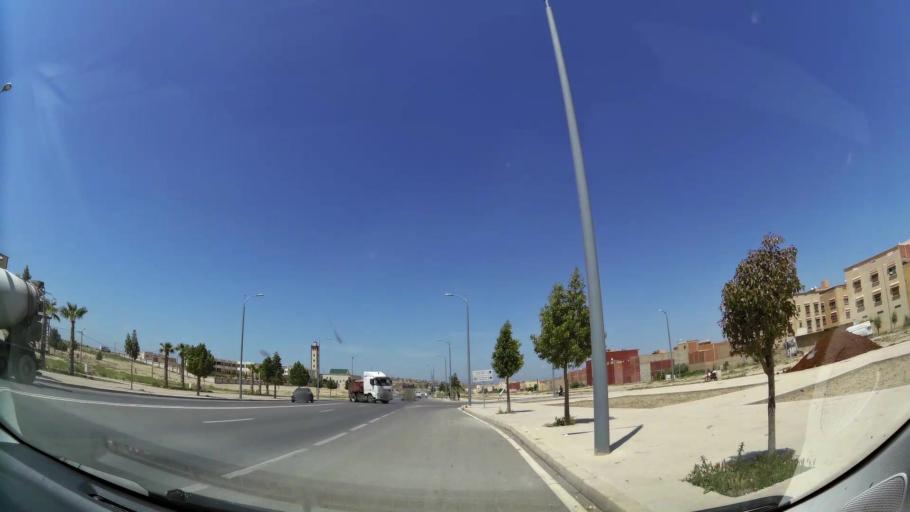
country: MA
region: Oriental
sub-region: Oujda-Angad
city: Oujda
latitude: 34.6876
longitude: -1.9444
